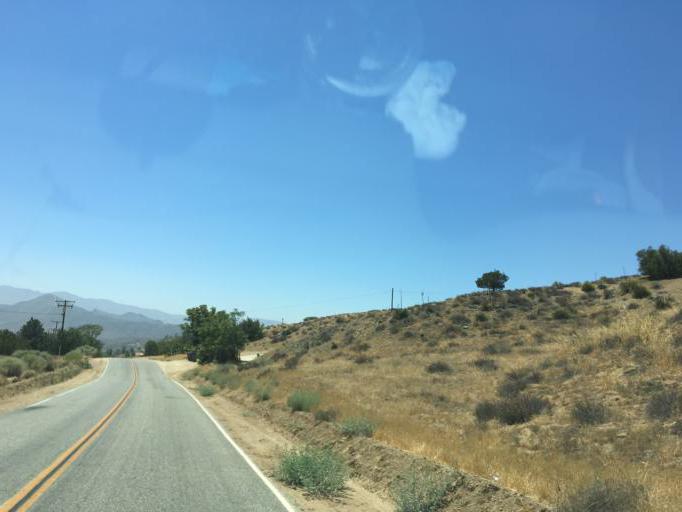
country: US
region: California
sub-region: Los Angeles County
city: Acton
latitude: 34.5150
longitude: -118.2153
